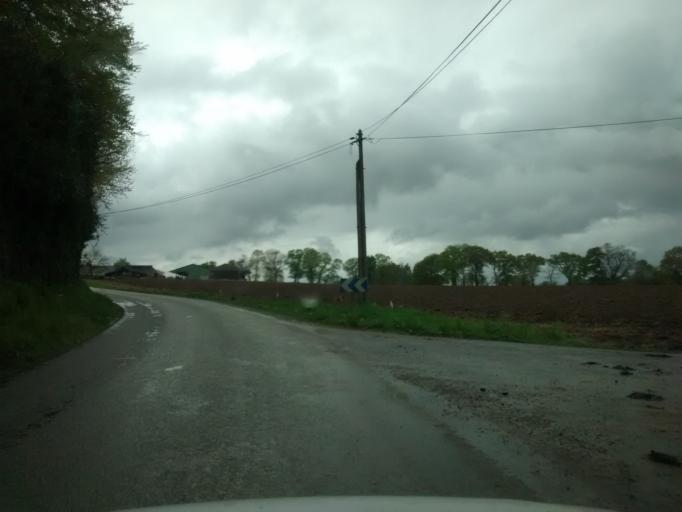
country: FR
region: Brittany
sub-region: Departement du Morbihan
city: Pleucadeuc
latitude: 47.7611
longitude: -2.3435
